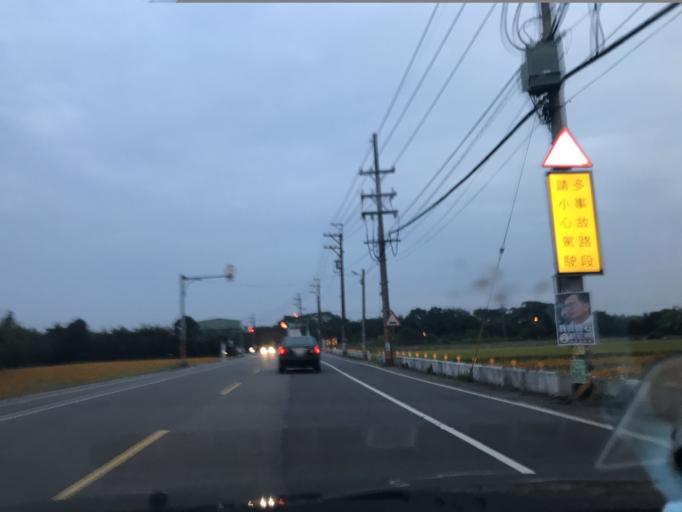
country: TW
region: Taiwan
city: Daxi
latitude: 24.9156
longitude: 121.2312
